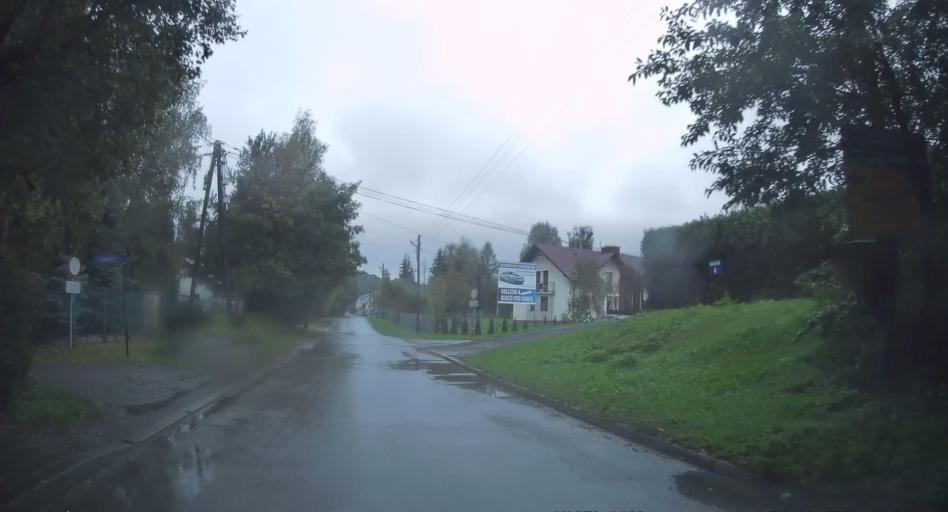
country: PL
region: Lesser Poland Voivodeship
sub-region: Powiat krakowski
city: Ochojno
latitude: 50.0027
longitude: 19.9934
